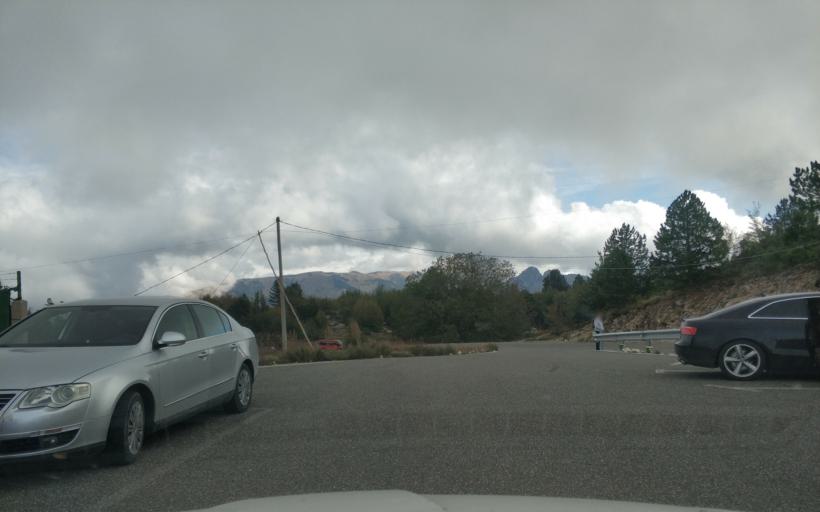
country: AL
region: Durres
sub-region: Rrethi i Krujes
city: Kruje
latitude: 41.5176
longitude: 19.8026
